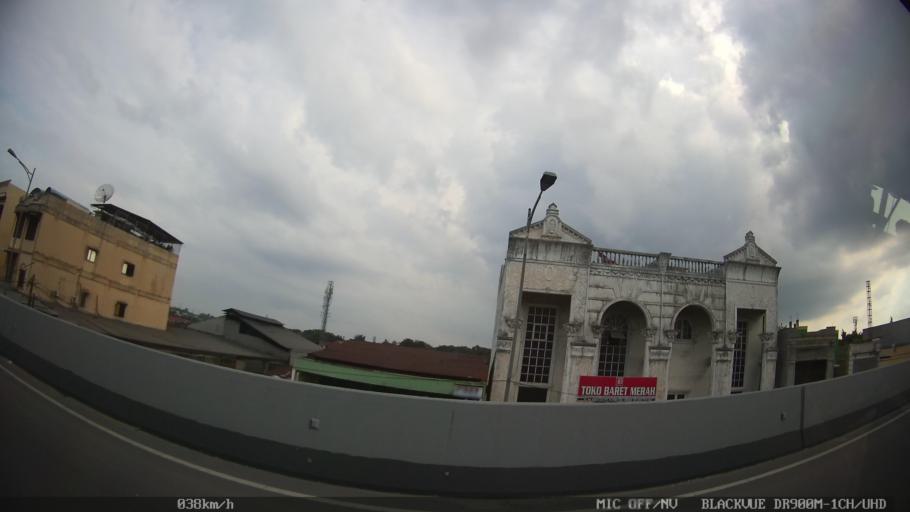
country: ID
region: North Sumatra
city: Deli Tua
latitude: 3.5406
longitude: 98.6558
